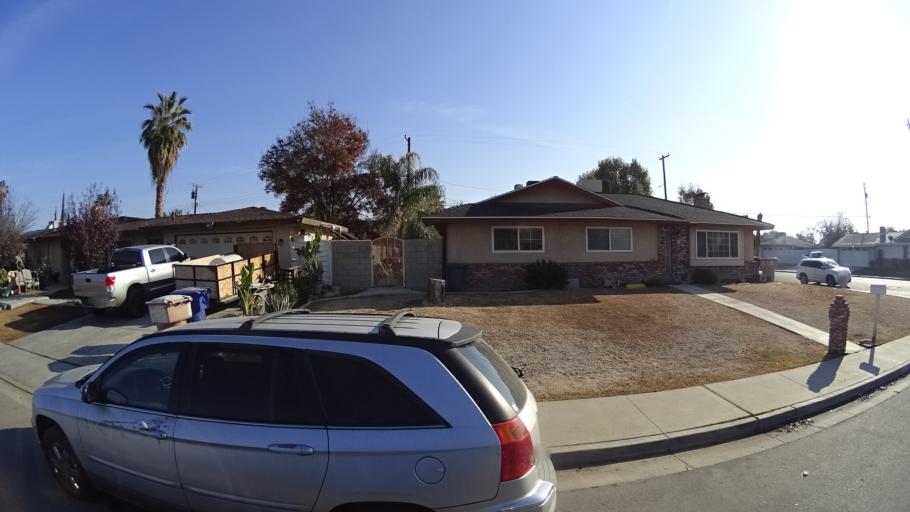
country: US
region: California
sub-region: Kern County
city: Greenfield
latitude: 35.3143
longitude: -119.0156
